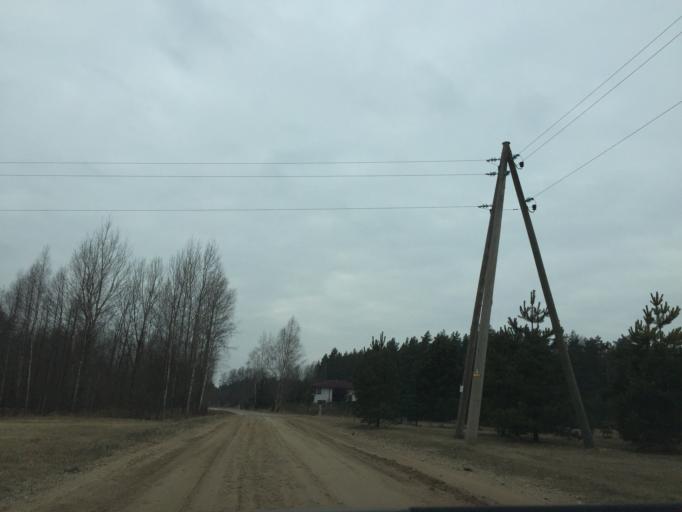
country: LV
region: Kekava
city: Balozi
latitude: 56.7918
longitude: 24.1455
